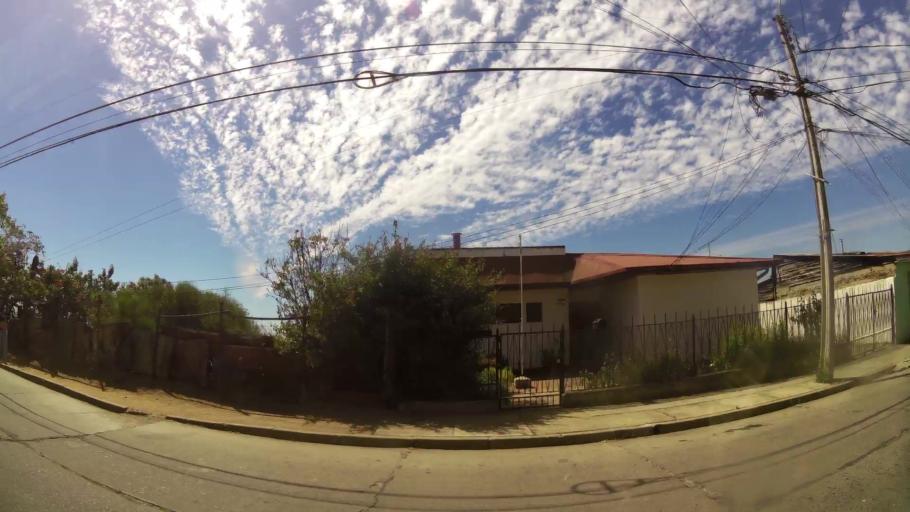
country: CL
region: Valparaiso
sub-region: Provincia de Valparaiso
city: Vina del Mar
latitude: -33.0370
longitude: -71.5812
